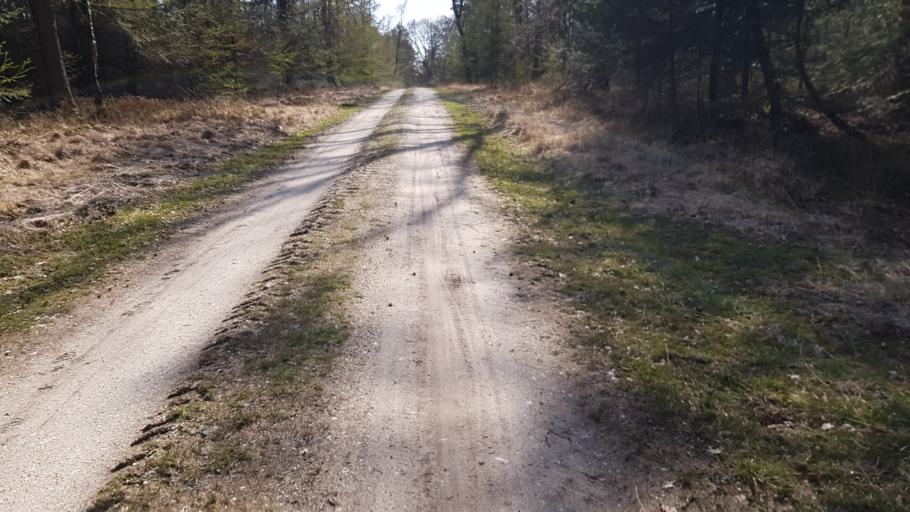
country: NL
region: Gelderland
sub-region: Gemeente Apeldoorn
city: Loenen
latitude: 52.0824
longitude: 5.9674
